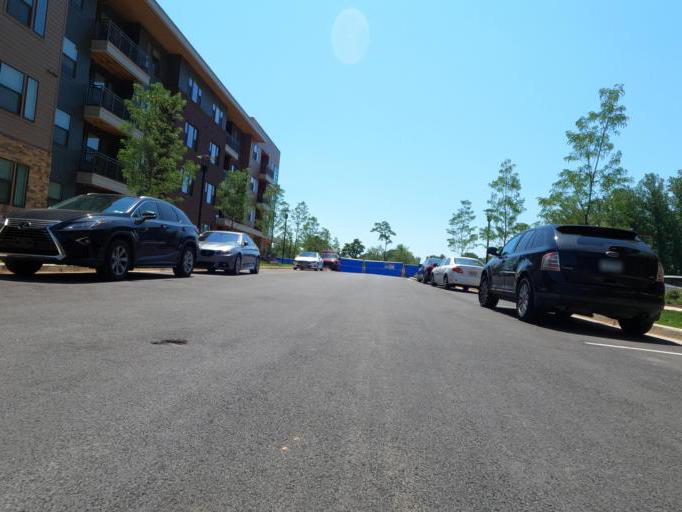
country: US
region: Maryland
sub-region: Montgomery County
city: Germantown
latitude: 39.2003
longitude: -77.2738
